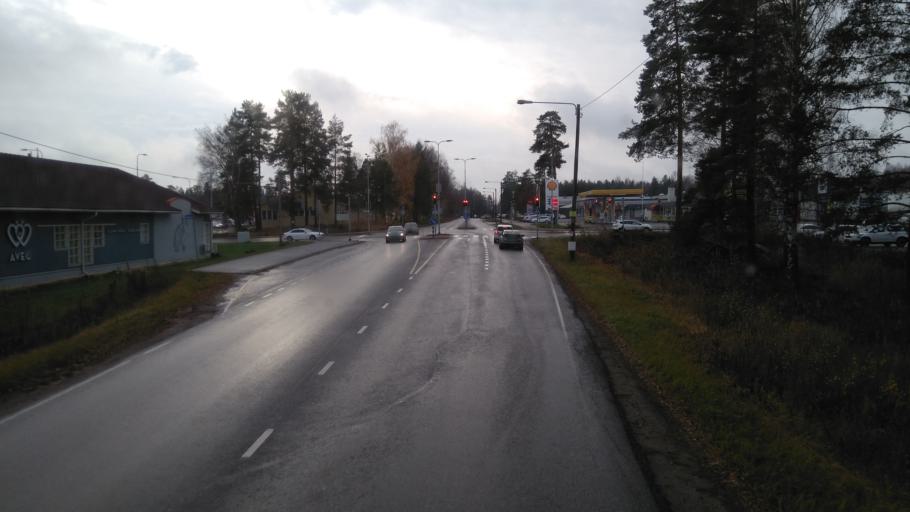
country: FI
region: Uusimaa
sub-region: Porvoo
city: Porvoo
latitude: 60.4037
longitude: 25.6889
